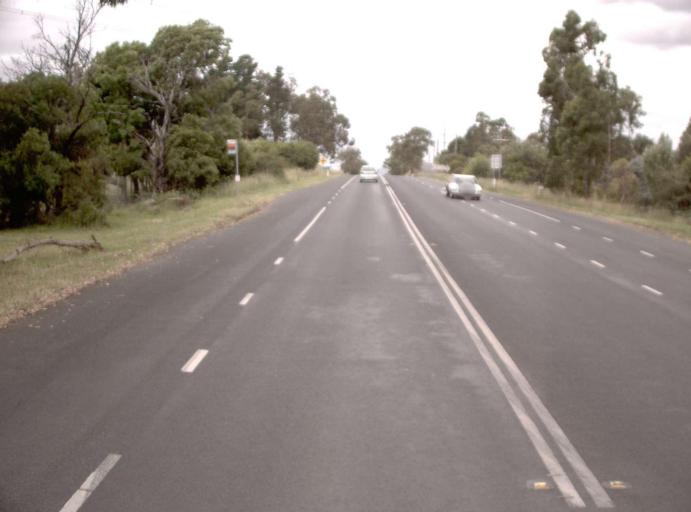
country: AU
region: Victoria
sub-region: Yarra Ranges
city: Woori Yallock
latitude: -37.7760
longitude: 145.4858
